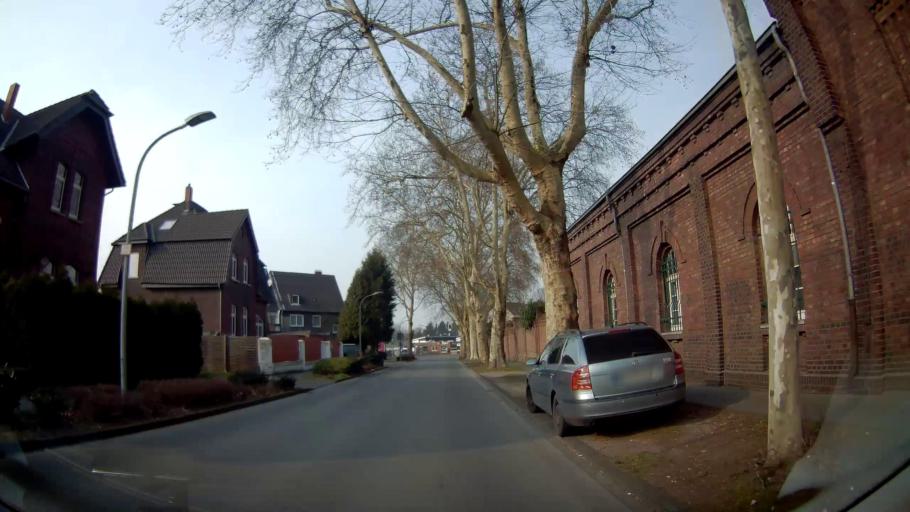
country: DE
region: North Rhine-Westphalia
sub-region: Regierungsbezirk Munster
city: Bottrop
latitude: 51.5314
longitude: 6.9312
